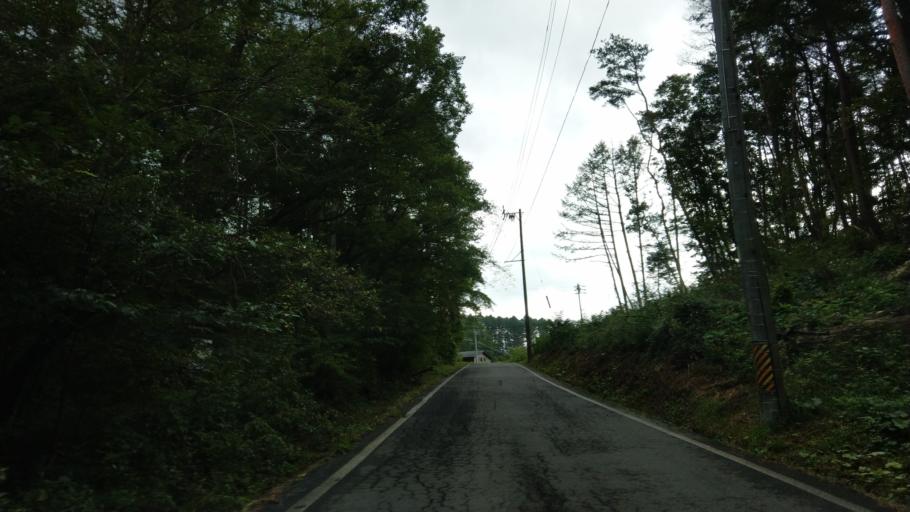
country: JP
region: Nagano
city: Komoro
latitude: 36.3061
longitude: 138.3909
